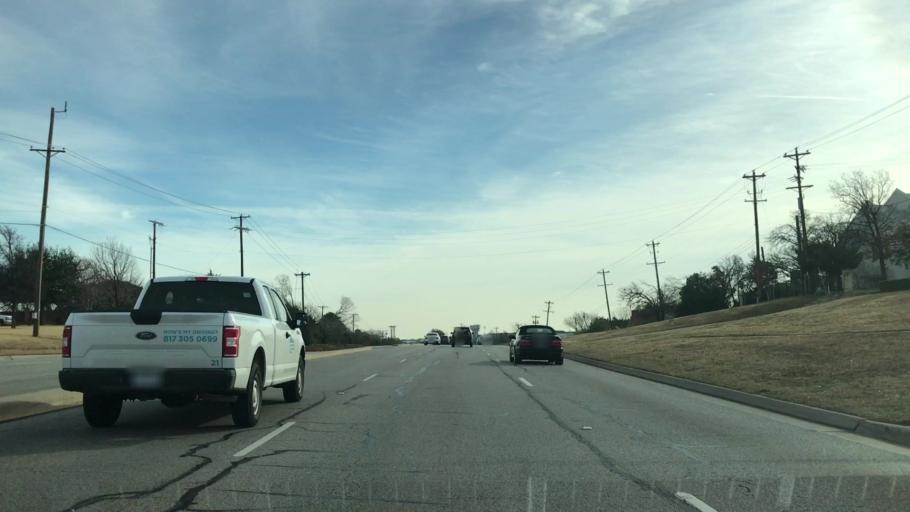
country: US
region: Texas
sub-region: Tarrant County
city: Southlake
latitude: 32.9414
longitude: -97.1498
